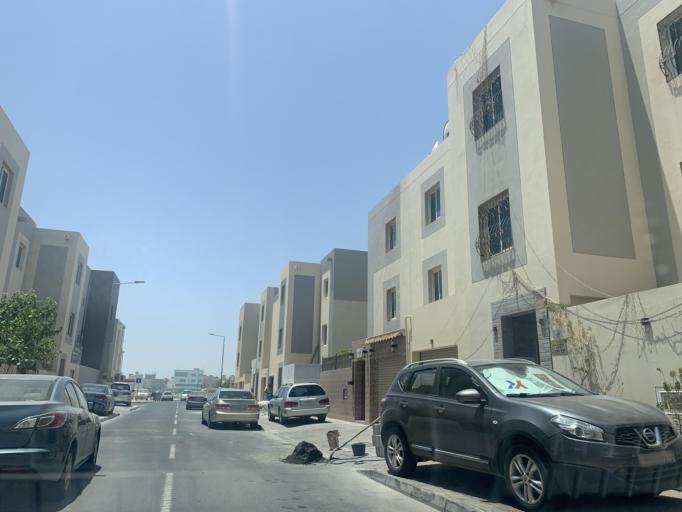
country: BH
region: Manama
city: Jidd Hafs
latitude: 26.2345
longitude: 50.4653
